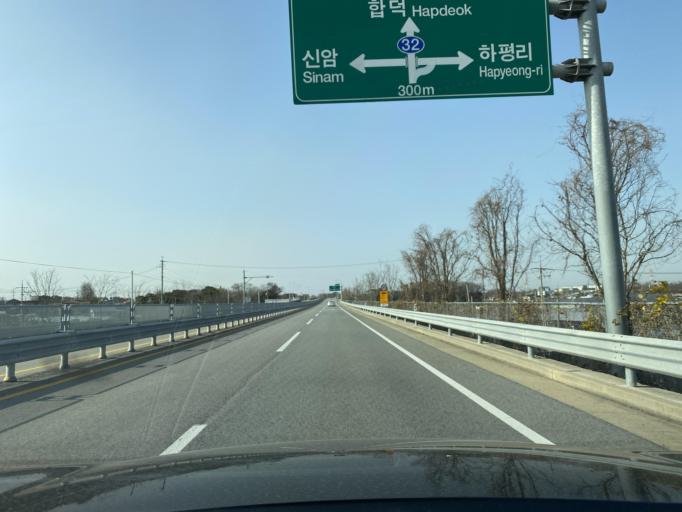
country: KR
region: Chungcheongnam-do
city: Yesan
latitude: 36.7579
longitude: 126.8270
